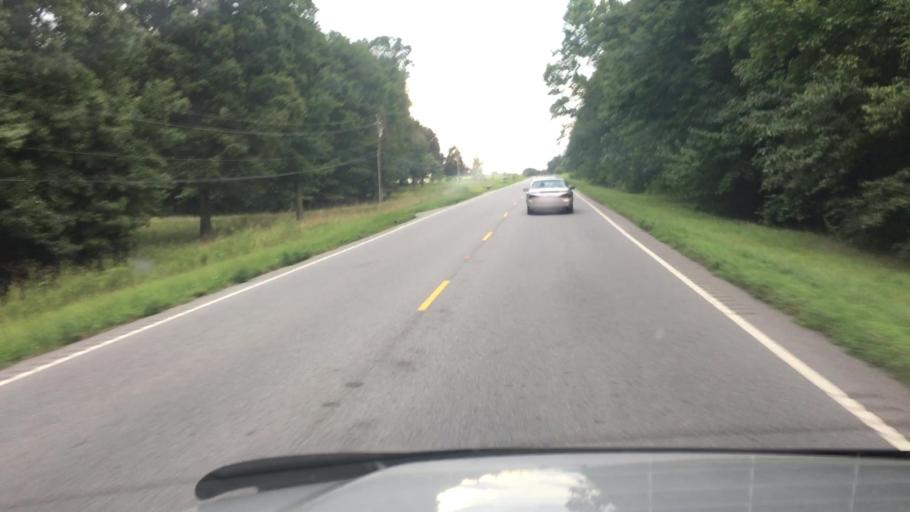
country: US
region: South Carolina
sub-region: Spartanburg County
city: Mayo
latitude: 35.1356
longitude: -81.8041
